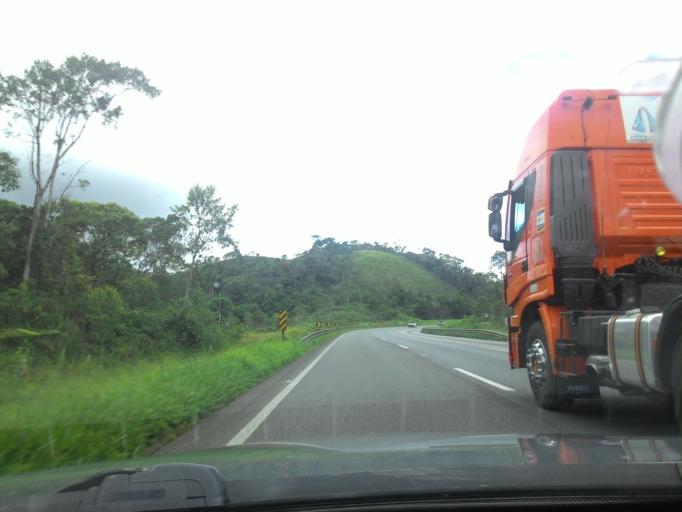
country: BR
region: Sao Paulo
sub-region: Cajati
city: Cajati
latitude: -24.9087
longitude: -48.2537
